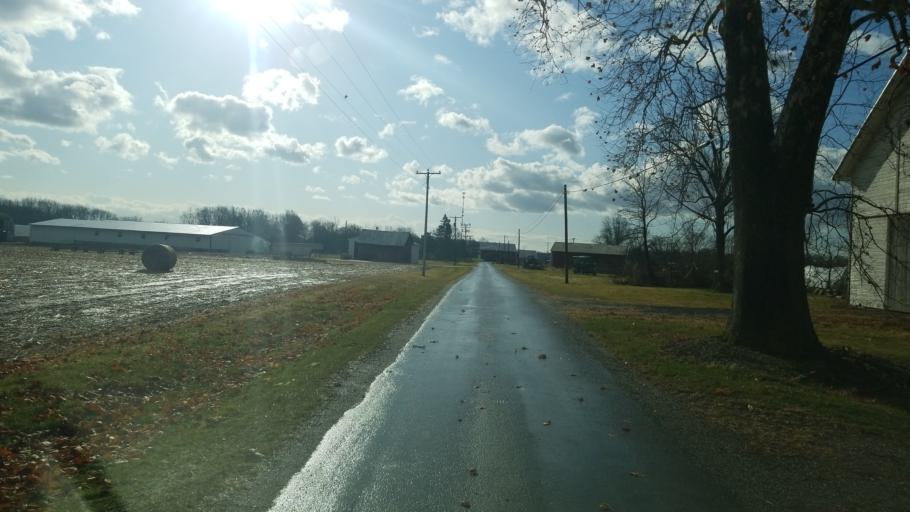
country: US
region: Ohio
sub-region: Marion County
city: Marion
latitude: 40.5371
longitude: -83.0714
